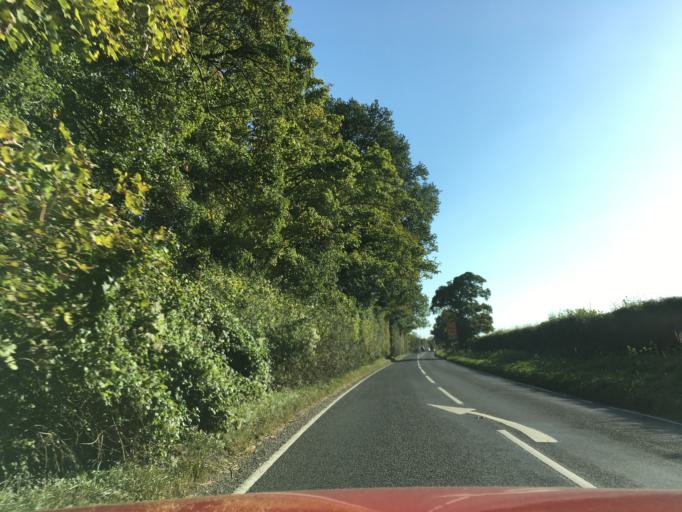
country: GB
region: England
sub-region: Hampshire
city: Swanmore
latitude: 50.9950
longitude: -1.1183
